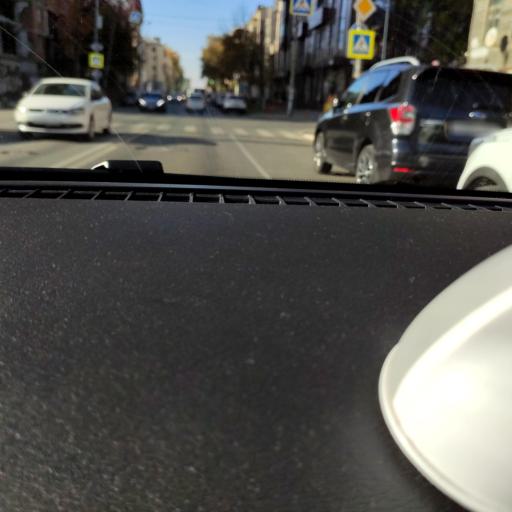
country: RU
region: Samara
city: Samara
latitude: 53.1960
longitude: 50.1111
